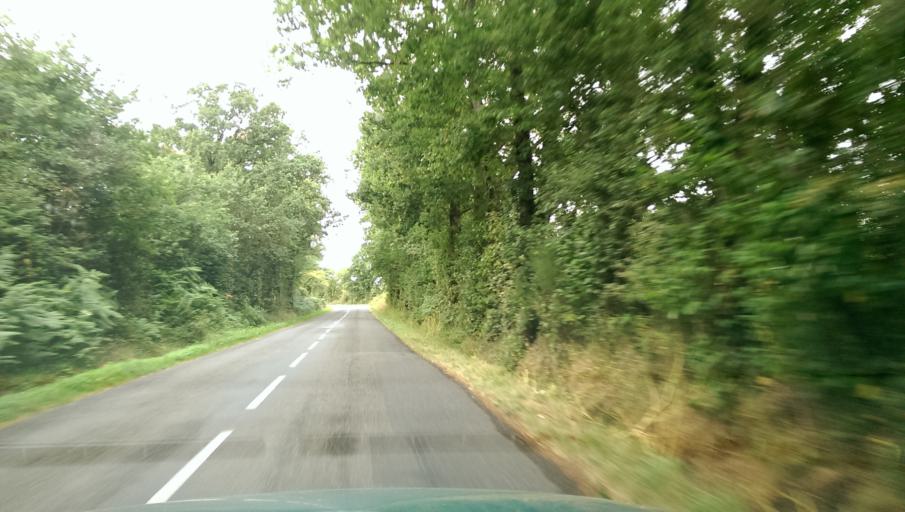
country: FR
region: Pays de la Loire
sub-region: Departement de la Loire-Atlantique
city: La Planche
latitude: 47.0011
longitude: -1.3964
